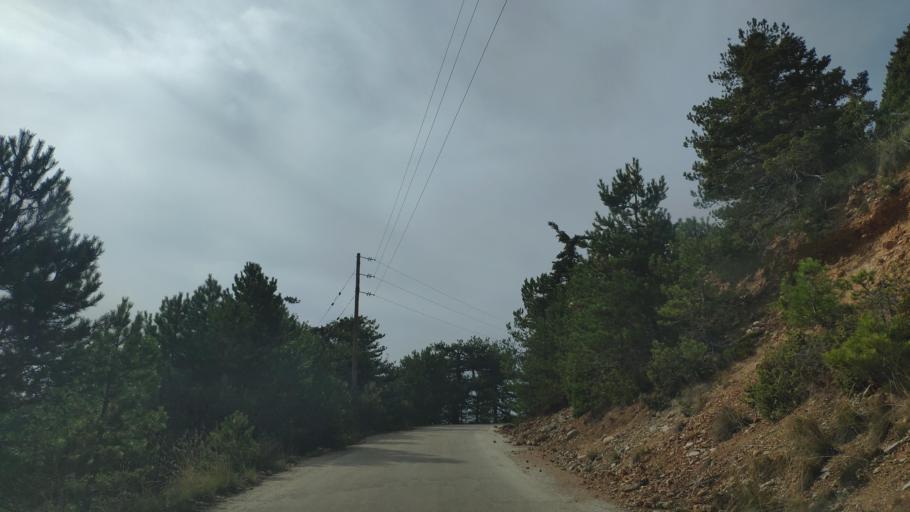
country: GR
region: West Greece
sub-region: Nomos Achaias
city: Aiyira
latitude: 38.0277
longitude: 22.3969
